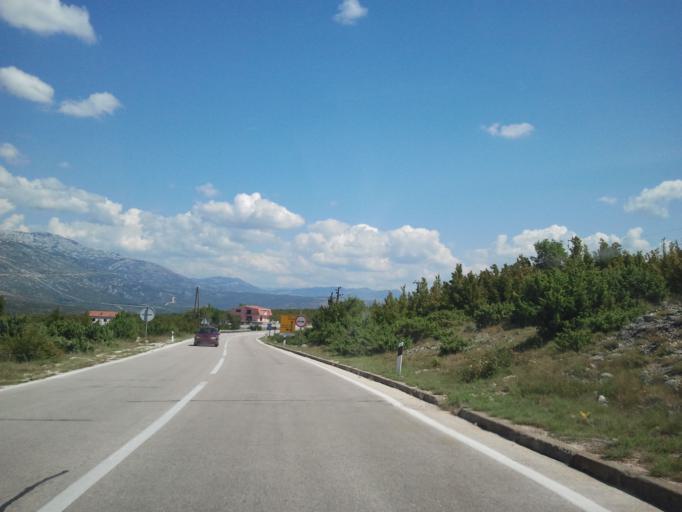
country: HR
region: Zadarska
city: Obrovac
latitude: 44.1940
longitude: 15.6777
